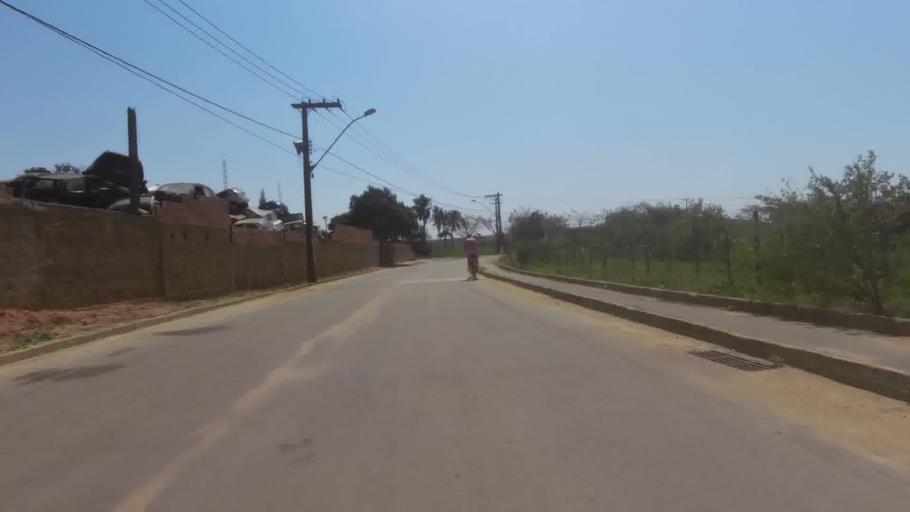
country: BR
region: Espirito Santo
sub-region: Itapemirim
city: Itapemirim
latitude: -21.0104
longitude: -40.8271
